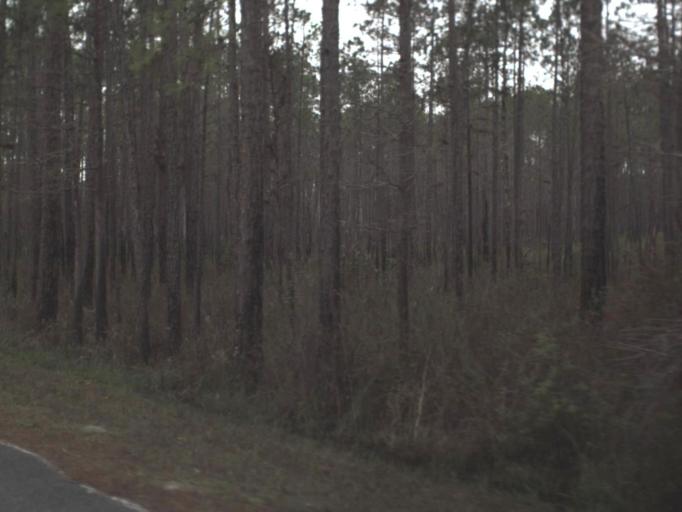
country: US
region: Florida
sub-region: Franklin County
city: Apalachicola
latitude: 29.9653
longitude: -84.9758
